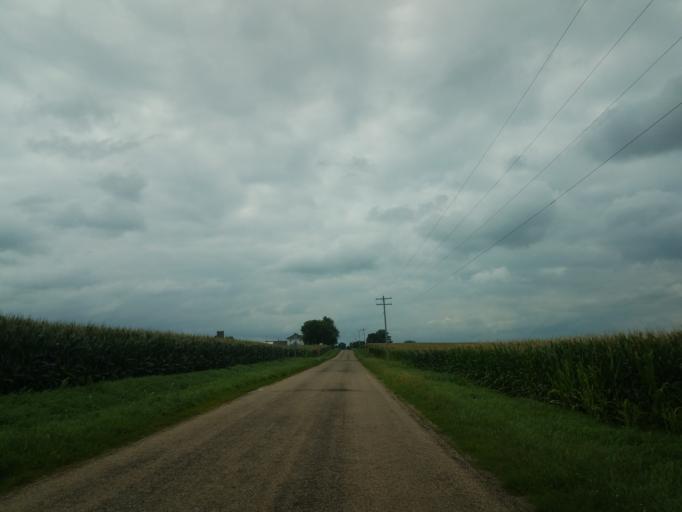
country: US
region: Illinois
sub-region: McLean County
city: Twin Grove
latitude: 40.4281
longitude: -89.0623
